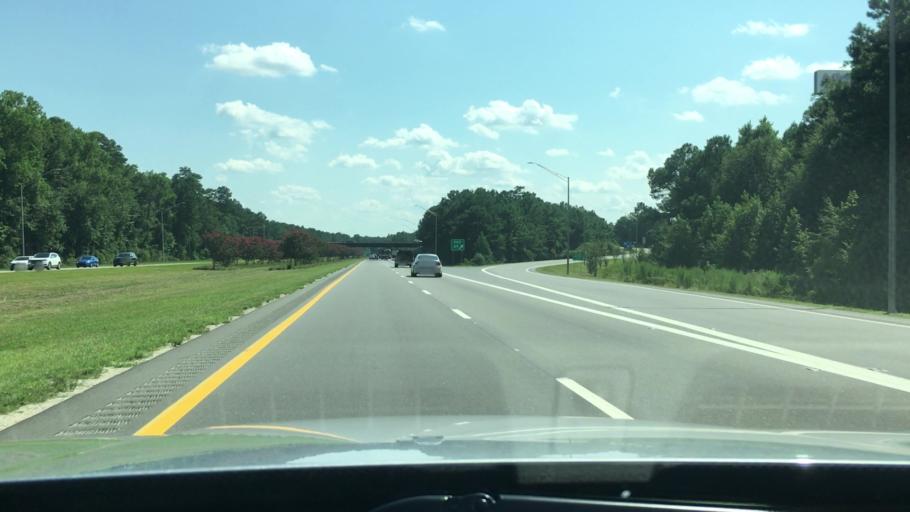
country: US
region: North Carolina
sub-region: Cumberland County
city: Vander
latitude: 35.0109
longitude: -78.8189
